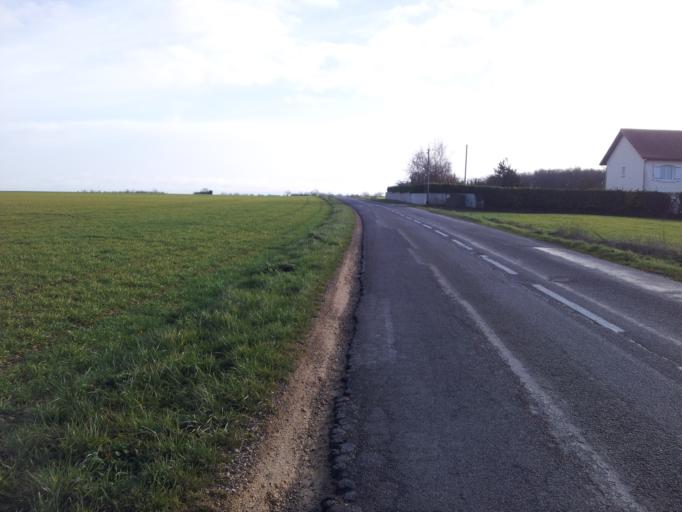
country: FR
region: Poitou-Charentes
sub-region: Departement de la Vienne
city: Avanton
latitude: 46.6617
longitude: 0.3192
